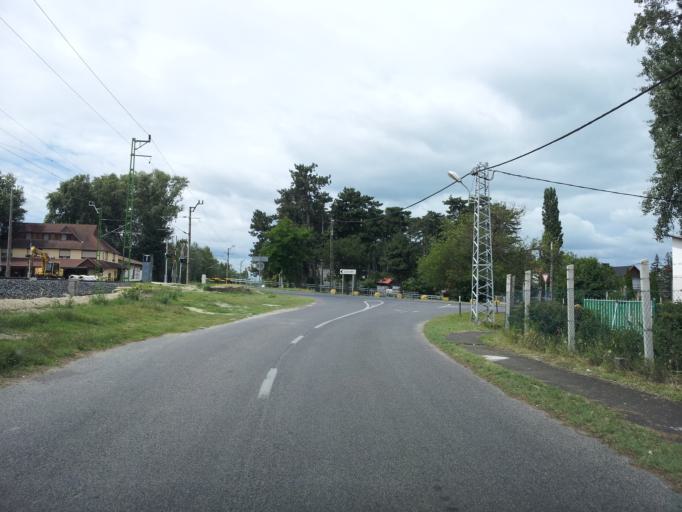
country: HU
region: Somogy
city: Siofok
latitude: 46.9185
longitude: 18.0830
